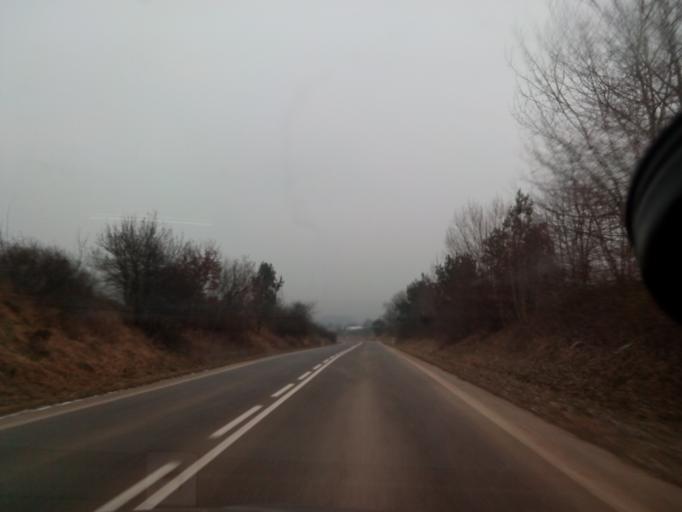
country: SK
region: Kosicky
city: Moldava nad Bodvou
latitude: 48.6742
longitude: 21.1090
